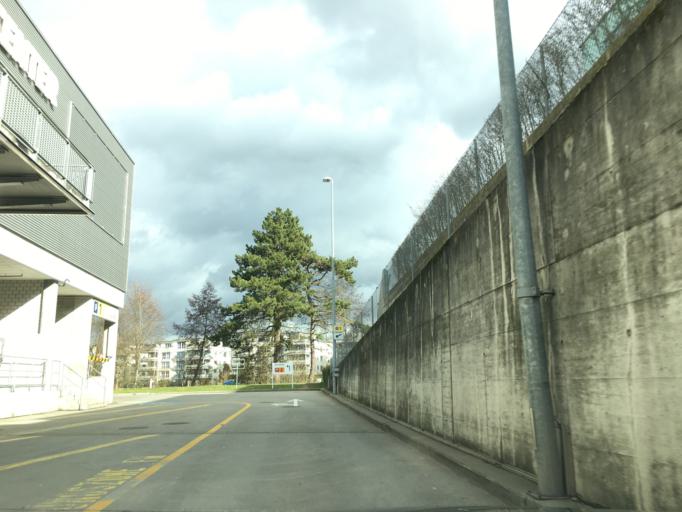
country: CH
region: Zurich
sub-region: Bezirk Buelach
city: Bachenbulach
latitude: 47.5099
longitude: 8.5413
